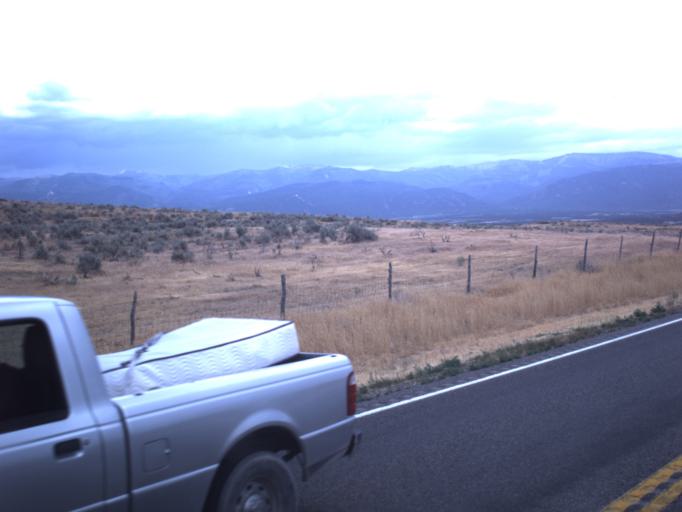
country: US
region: Utah
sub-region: Sanpete County
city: Moroni
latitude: 39.4998
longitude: -111.5656
